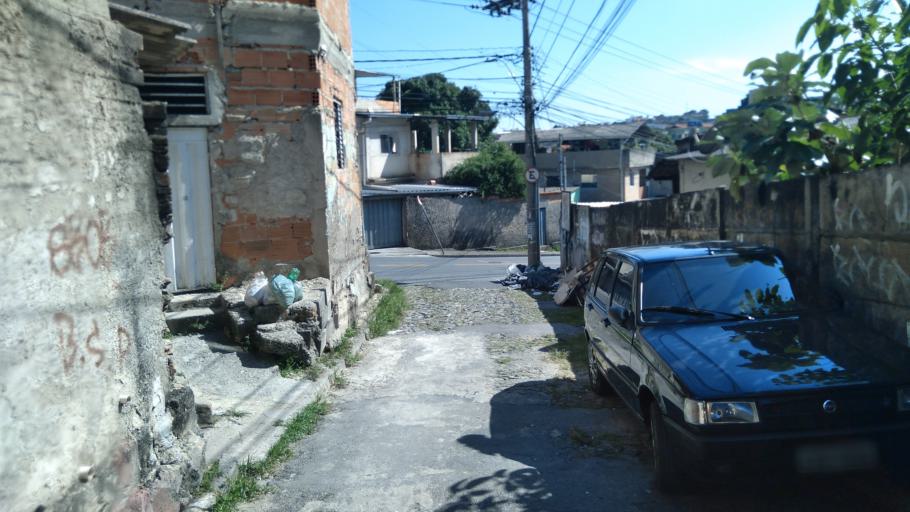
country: BR
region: Minas Gerais
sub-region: Belo Horizonte
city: Belo Horizonte
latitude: -19.8674
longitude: -43.9211
